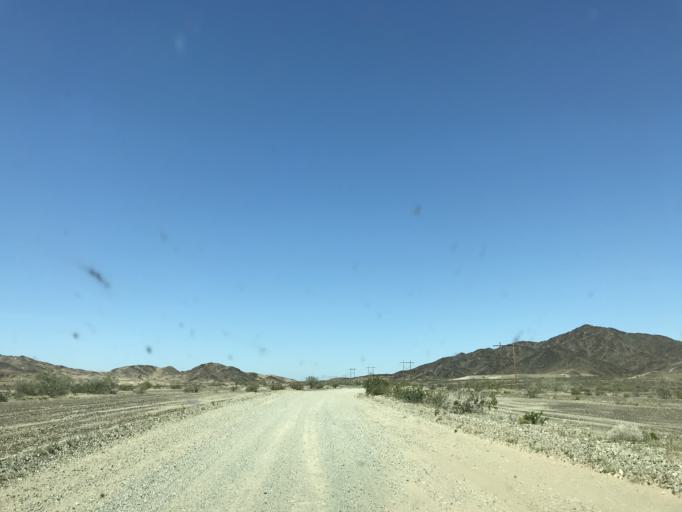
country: US
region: California
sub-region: Riverside County
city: Mesa Verde
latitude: 33.4936
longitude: -114.8183
